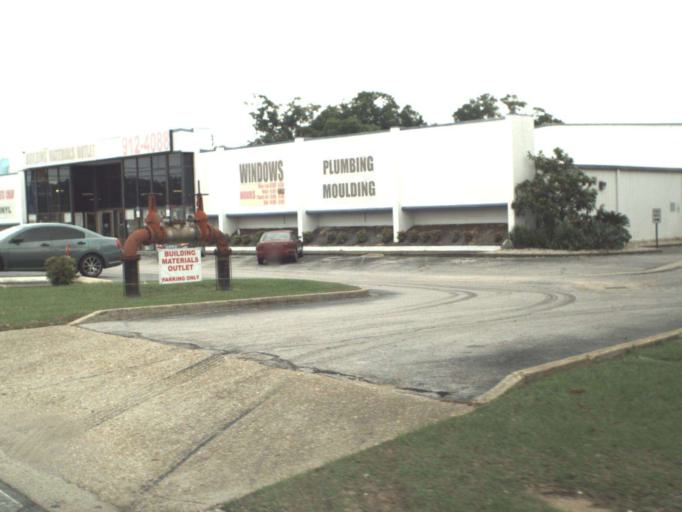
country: US
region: Florida
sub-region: Escambia County
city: Brent
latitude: 30.4740
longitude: -87.2253
